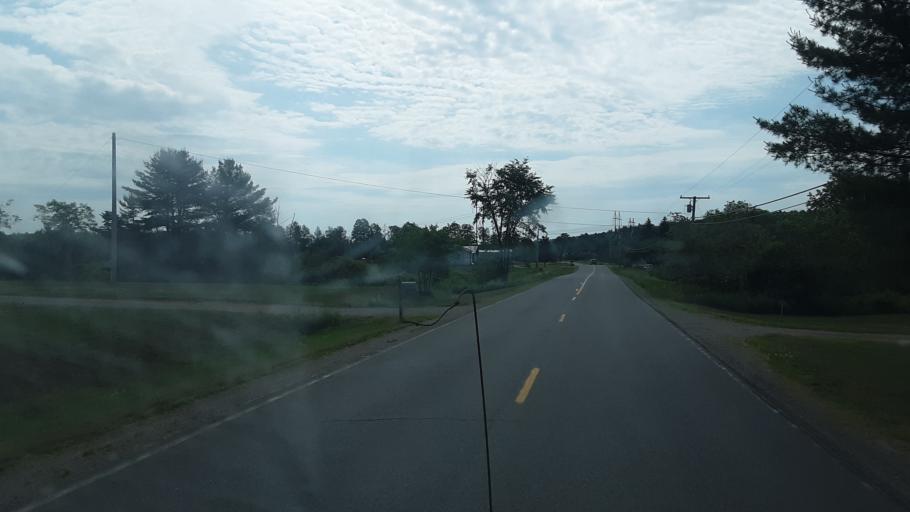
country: US
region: Maine
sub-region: Waldo County
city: Frankfort
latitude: 44.6163
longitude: -68.9432
